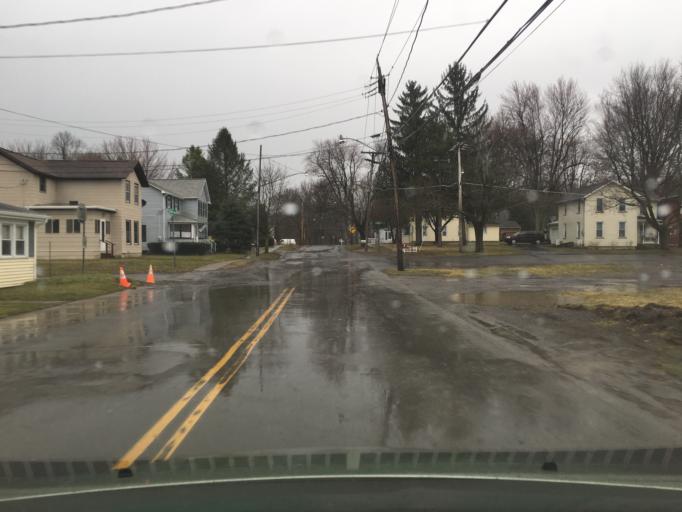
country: US
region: New York
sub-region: Ontario County
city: Shortsville
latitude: 42.9546
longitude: -77.2205
